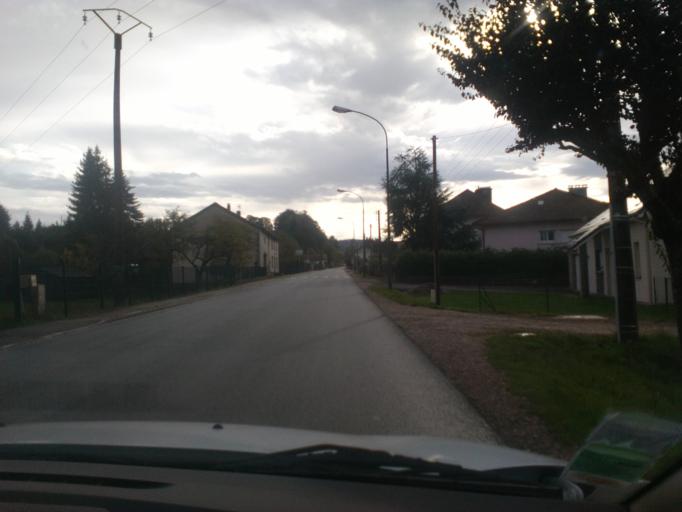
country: FR
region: Lorraine
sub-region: Departement des Vosges
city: Corcieux
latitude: 48.1689
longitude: 6.8877
